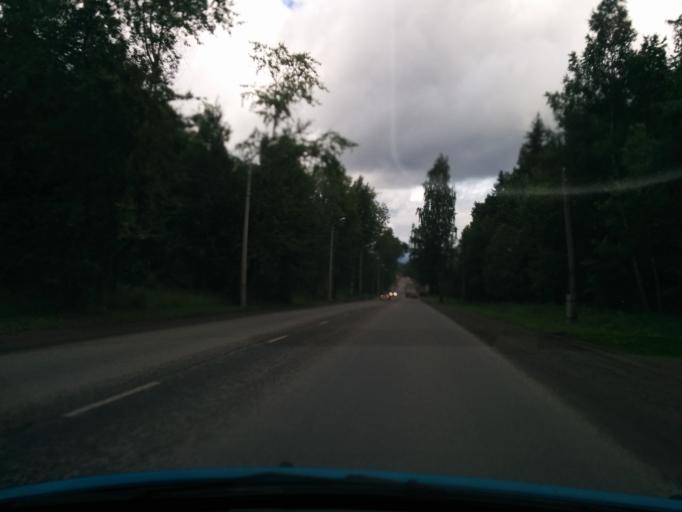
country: RU
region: Perm
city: Kondratovo
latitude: 58.0450
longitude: 56.0765
